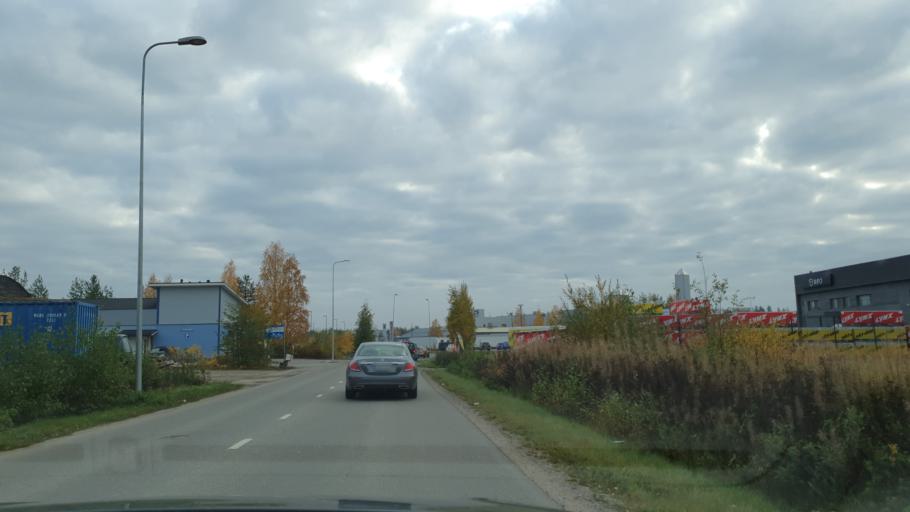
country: FI
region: Lapland
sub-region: Rovaniemi
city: Rovaniemi
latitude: 66.4928
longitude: 25.6802
